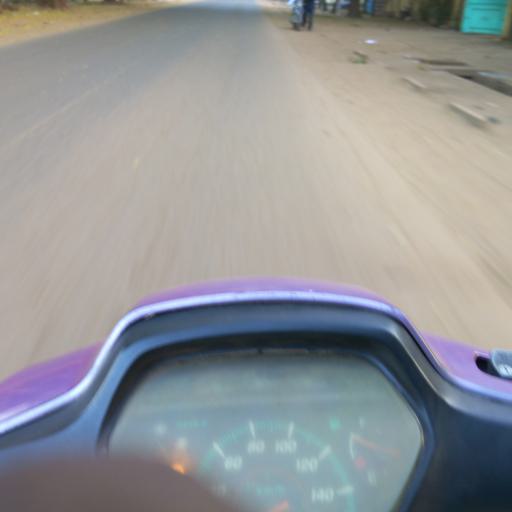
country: ML
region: Bamako
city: Bamako
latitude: 12.6522
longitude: -8.0134
